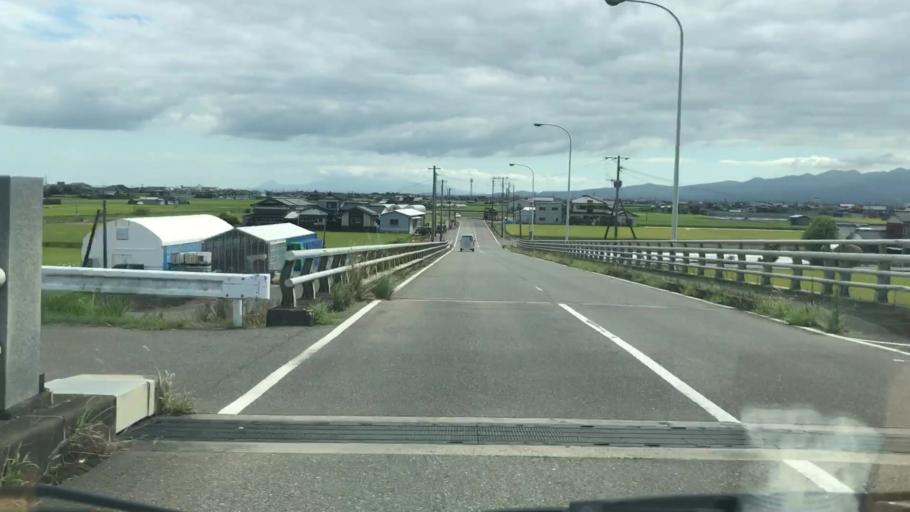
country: JP
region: Saga Prefecture
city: Saga-shi
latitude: 33.1991
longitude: 130.1813
